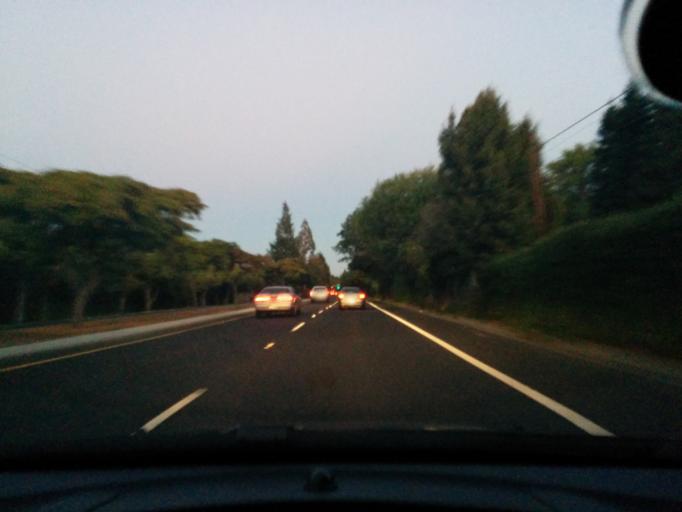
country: US
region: California
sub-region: Santa Clara County
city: Mountain View
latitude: 37.3998
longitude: -122.0889
